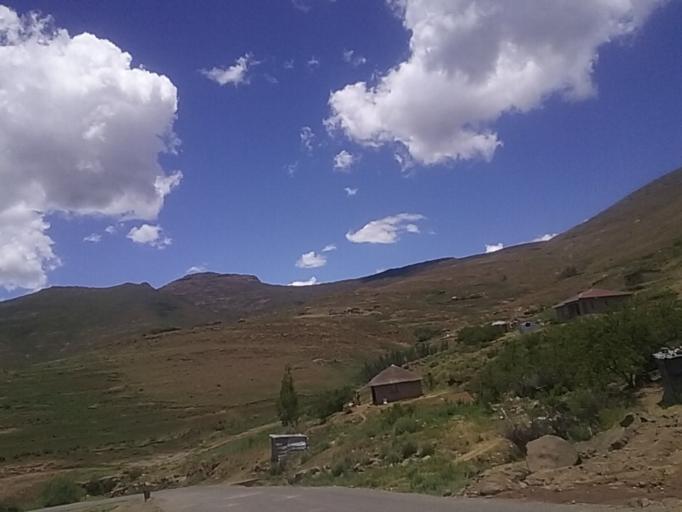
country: LS
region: Qacha's Nek
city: Qacha's Nek
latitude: -30.1683
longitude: 28.2066
